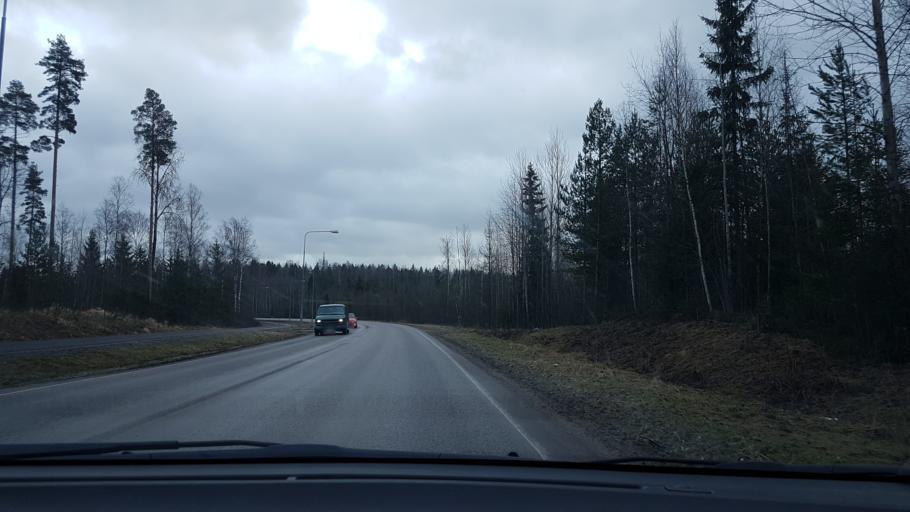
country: FI
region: Uusimaa
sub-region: Helsinki
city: Tuusula
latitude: 60.3733
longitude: 25.0619
